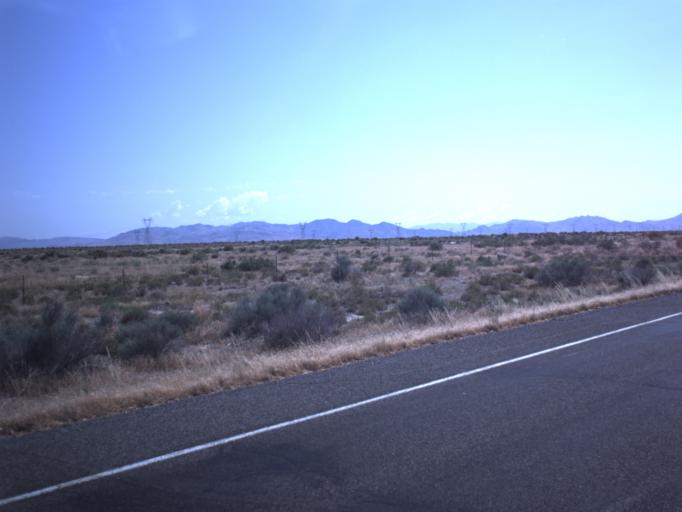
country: US
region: Utah
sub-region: Millard County
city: Delta
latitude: 39.4866
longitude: -112.5395
